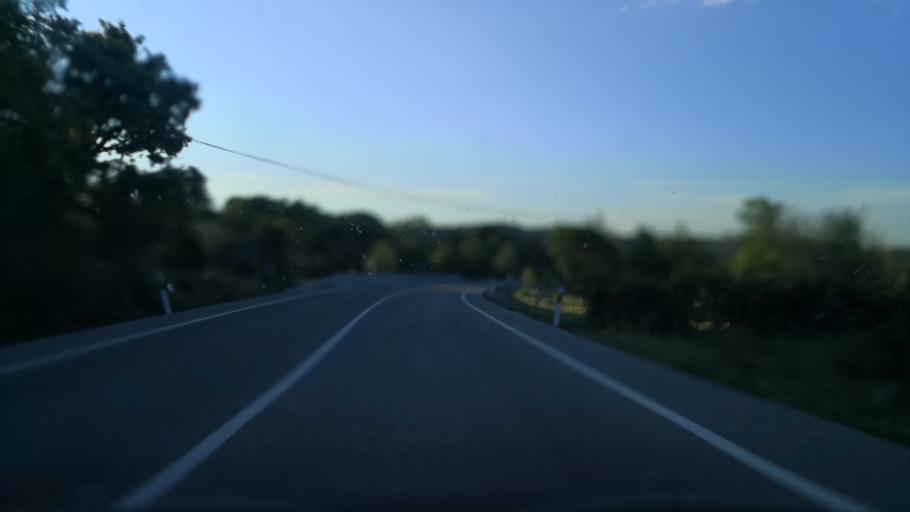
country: PT
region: Portalegre
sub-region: Portalegre
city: Sao Juliao
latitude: 39.3544
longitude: -7.2745
